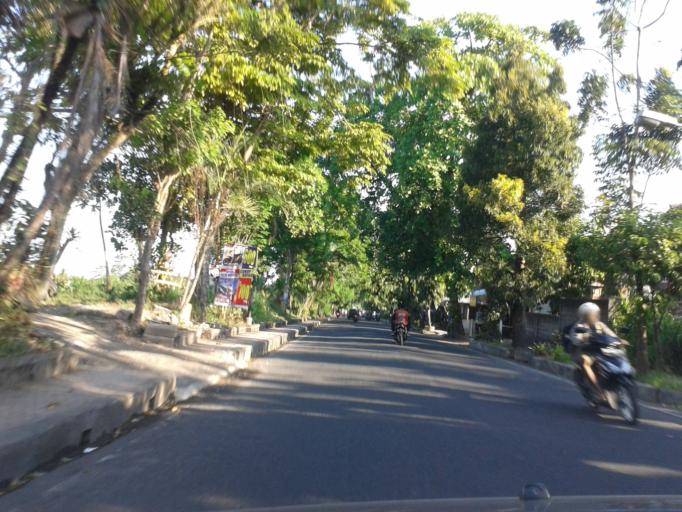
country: ID
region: Bali
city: Klungkung
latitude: -8.5221
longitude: 115.4019
